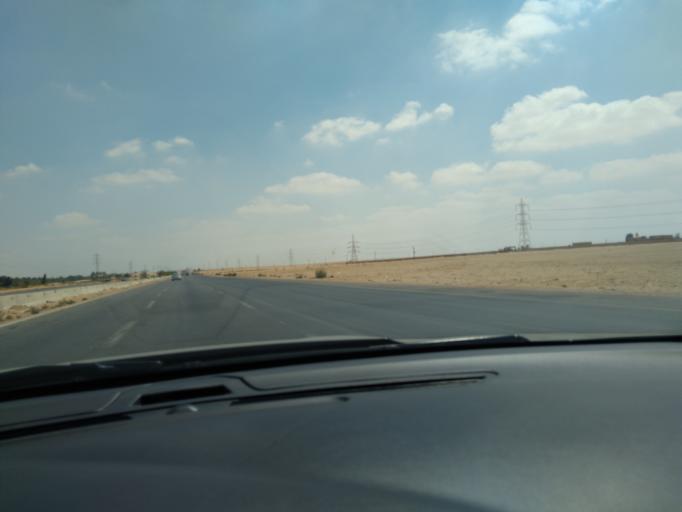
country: EG
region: Al Isma'iliyah
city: At Tall al Kabir
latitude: 30.3594
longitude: 31.9028
